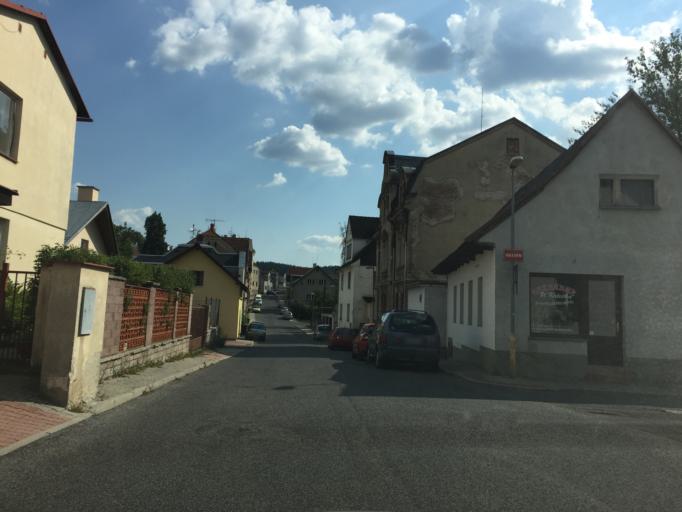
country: CZ
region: Liberecky
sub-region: Okres Jablonec nad Nisou
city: Jablonec nad Nisou
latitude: 50.7291
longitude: 15.1787
